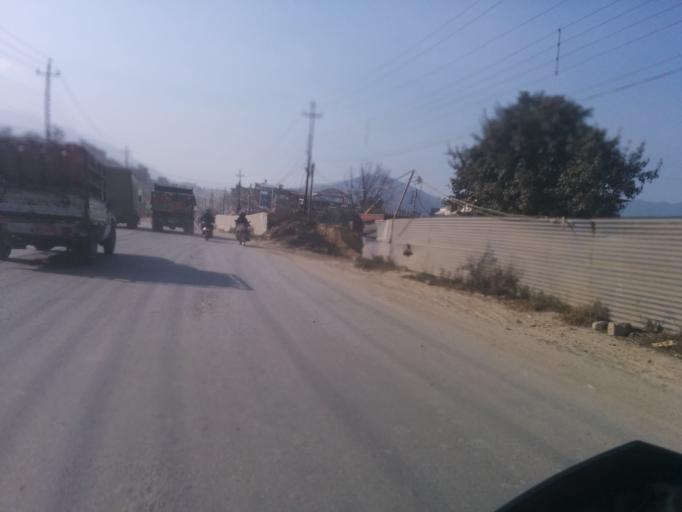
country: NP
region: Central Region
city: Kirtipur
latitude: 27.6880
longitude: 85.2896
